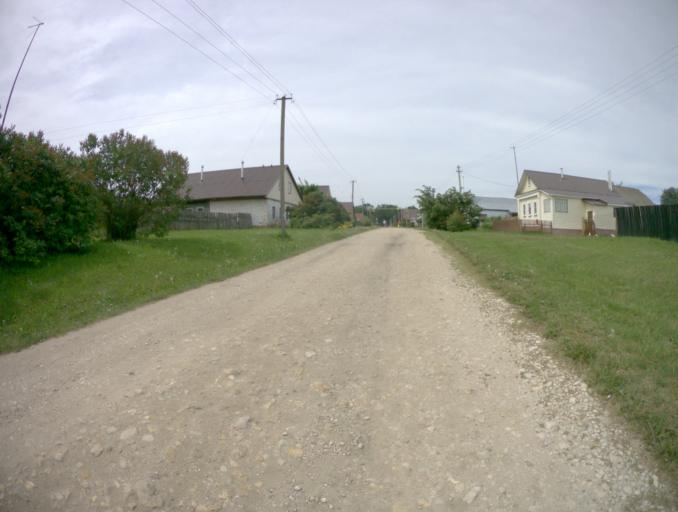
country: RU
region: Vladimir
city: Stavrovo
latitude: 56.1697
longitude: 39.9784
